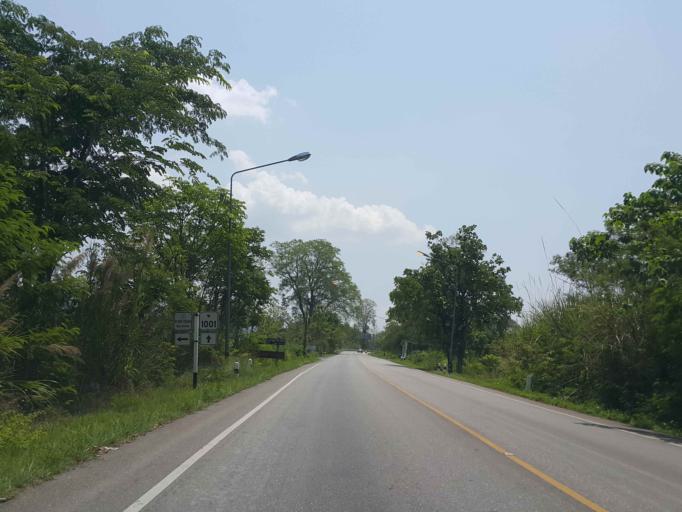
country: TH
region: Chiang Mai
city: Mae Taeng
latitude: 19.0997
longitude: 99.0766
